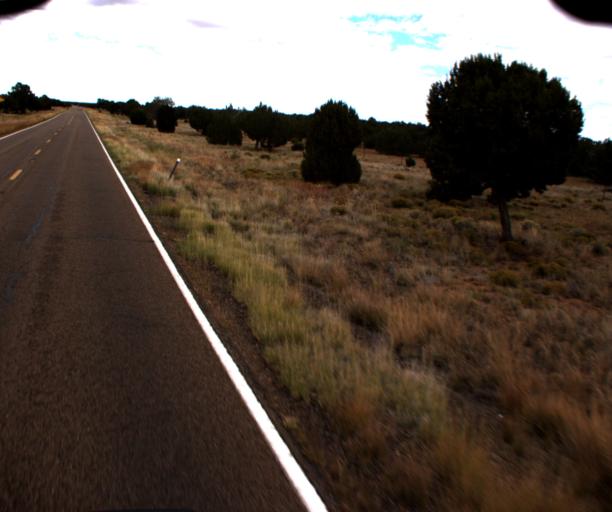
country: US
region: Arizona
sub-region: Navajo County
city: Heber-Overgaard
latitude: 34.4827
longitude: -110.4629
